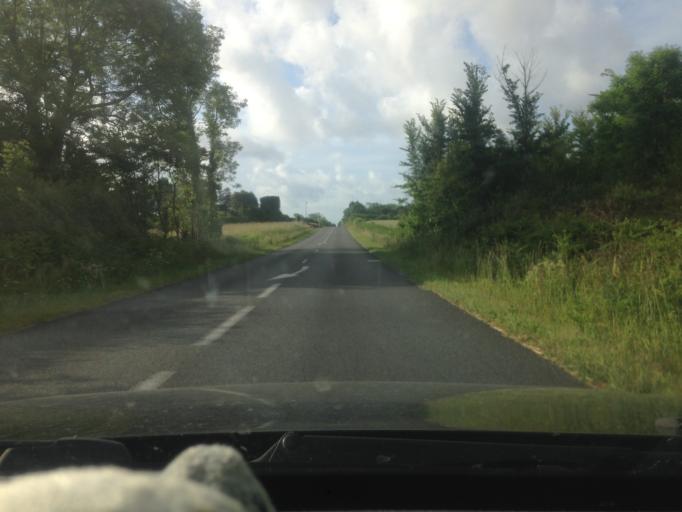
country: FR
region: Brittany
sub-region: Departement du Morbihan
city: Plouharnel
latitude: 47.6185
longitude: -3.1332
